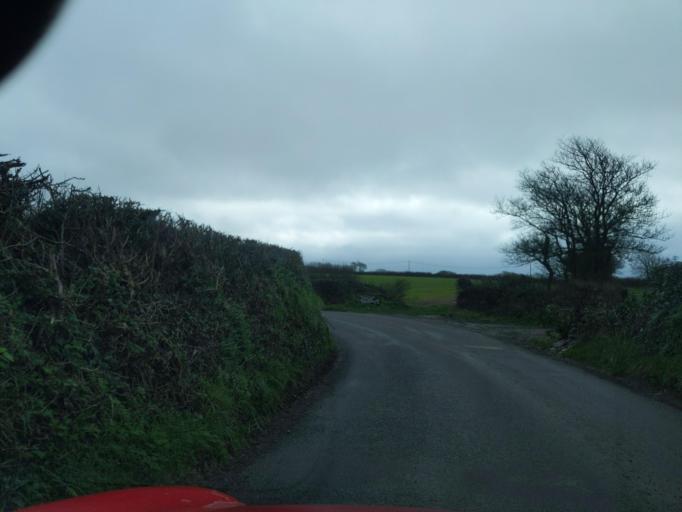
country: GB
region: England
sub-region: Devon
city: Wembury
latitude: 50.3298
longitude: -4.0945
